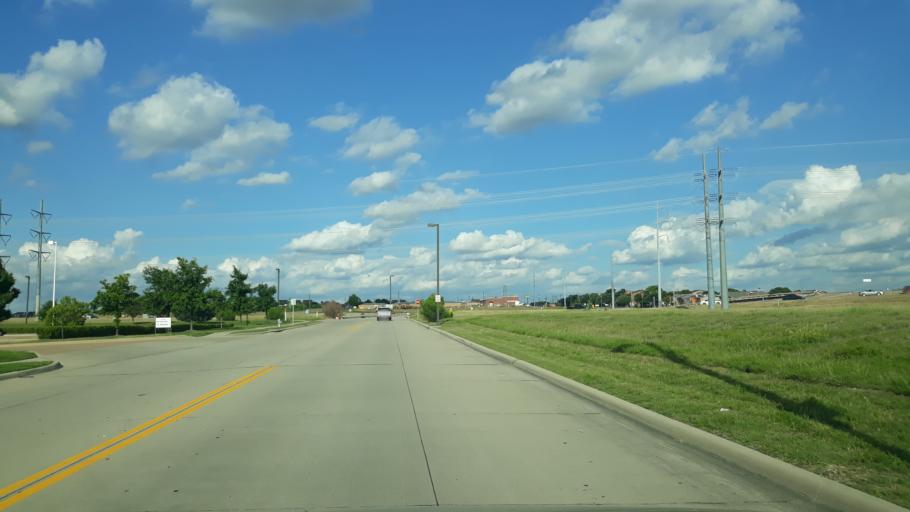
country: US
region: Texas
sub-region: Tarrant County
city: Euless
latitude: 32.8583
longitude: -97.0155
